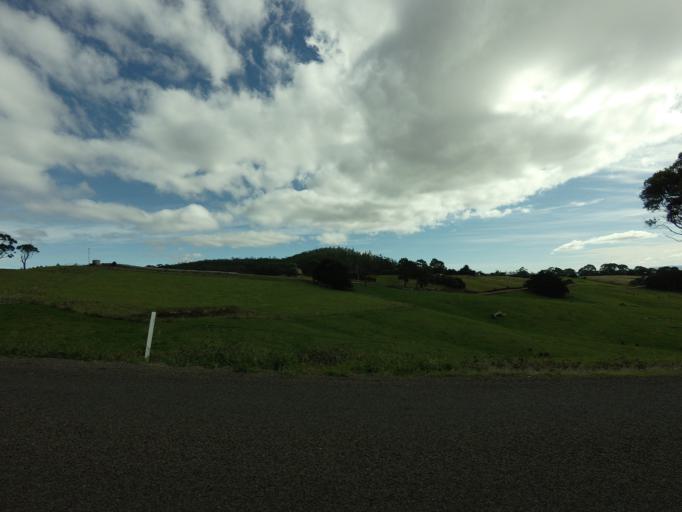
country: AU
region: Tasmania
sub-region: Clarence
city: Sandford
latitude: -43.0666
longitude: 147.7464
